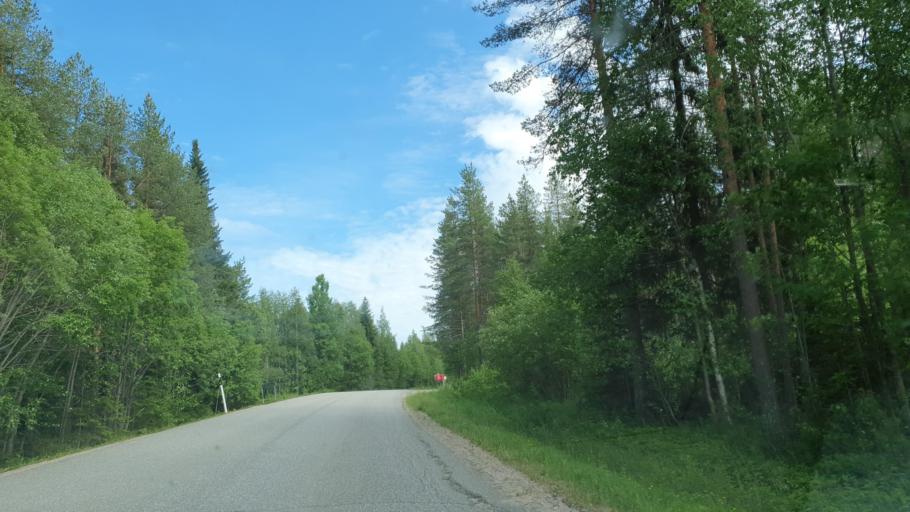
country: FI
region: Kainuu
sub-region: Kehys-Kainuu
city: Suomussalmi
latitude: 64.5544
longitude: 29.2061
